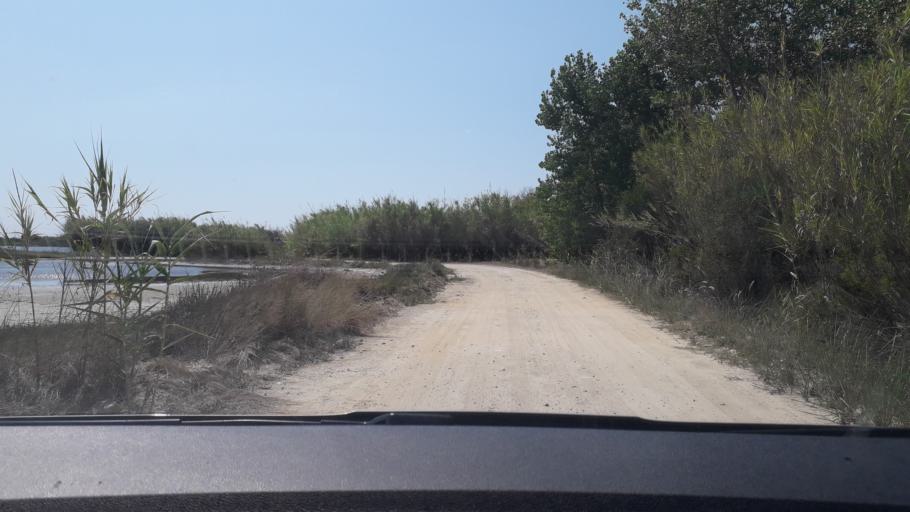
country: GR
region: Ionian Islands
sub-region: Nomos Kerkyras
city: Agios Matthaios
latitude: 39.4554
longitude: 19.8801
